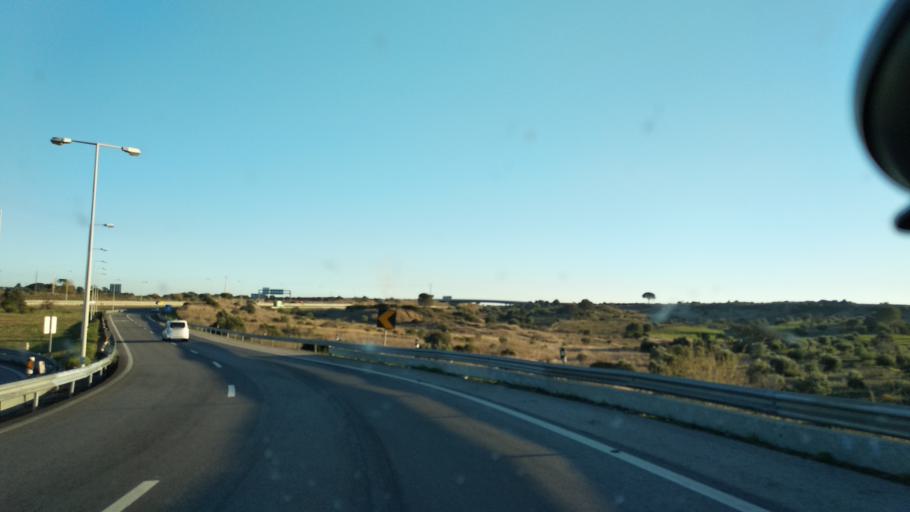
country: PT
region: Santarem
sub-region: Alcanena
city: Alcanena
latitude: 39.4757
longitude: -8.6322
